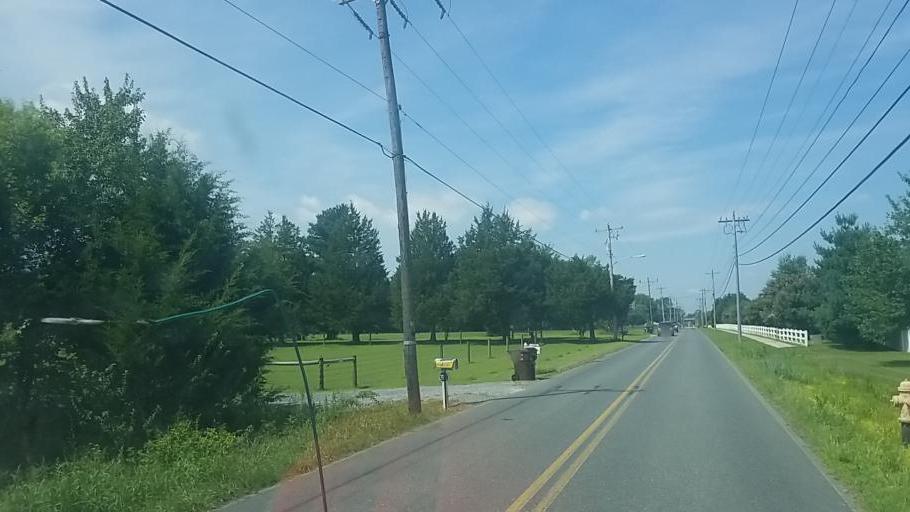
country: US
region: Maryland
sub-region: Caroline County
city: Denton
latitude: 38.8841
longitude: -75.8066
